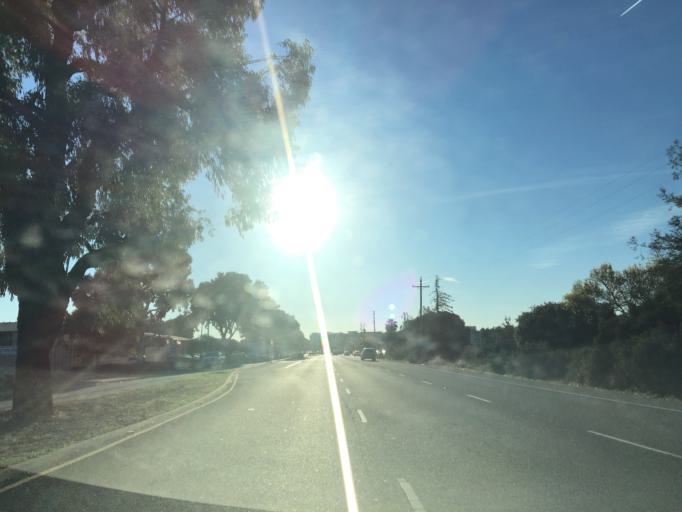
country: US
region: California
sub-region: San Mateo County
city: Redwood City
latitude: 37.4966
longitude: -122.2370
